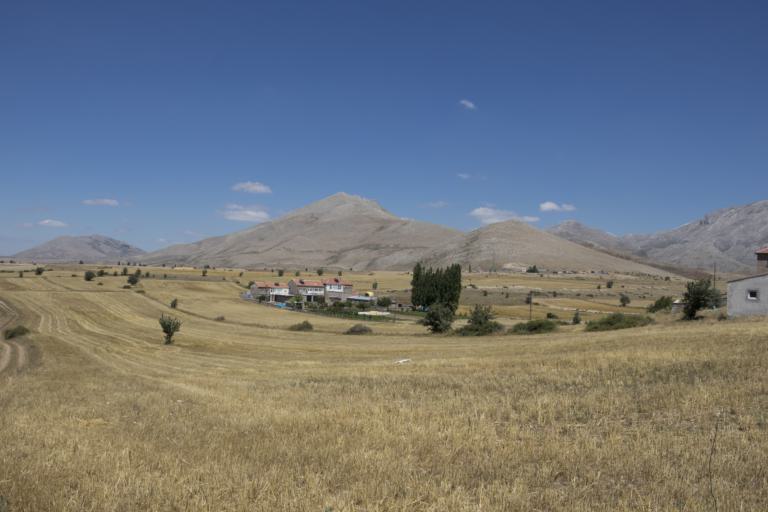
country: TR
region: Kayseri
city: Toklar
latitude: 38.4089
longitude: 36.0831
